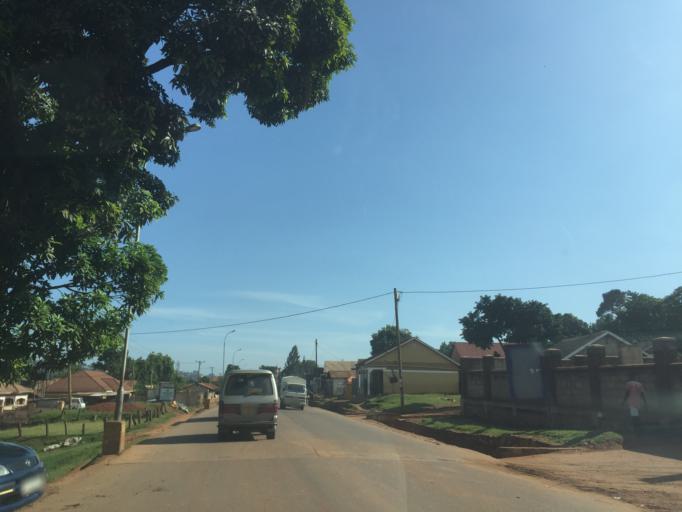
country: UG
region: Central Region
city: Kampala Central Division
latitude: 0.3665
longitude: 32.5695
